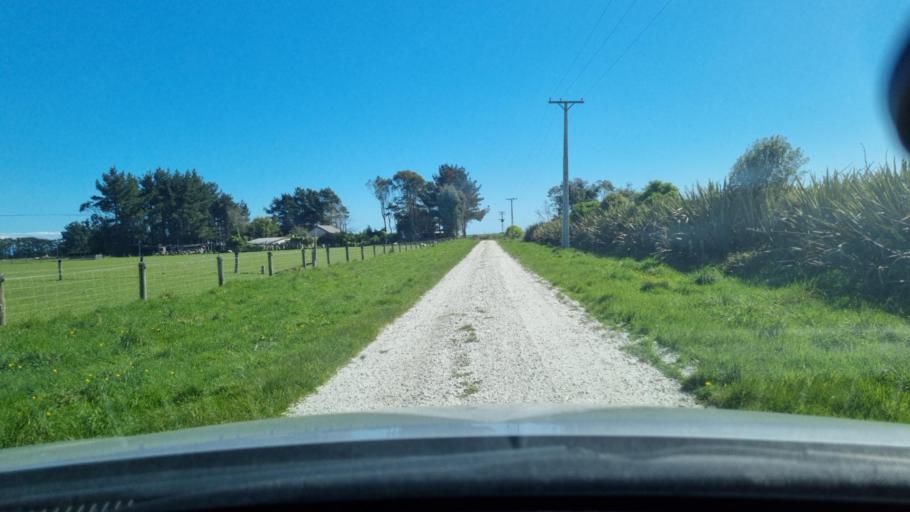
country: NZ
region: Southland
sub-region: Invercargill City
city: Invercargill
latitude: -46.3918
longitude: 168.2940
